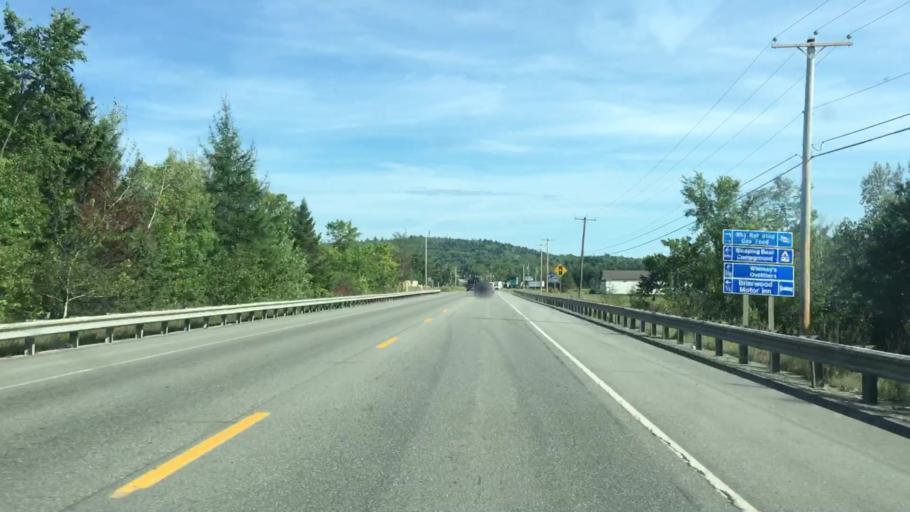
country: US
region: Maine
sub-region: Penobscot County
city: Lincoln
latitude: 45.3558
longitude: -68.5374
